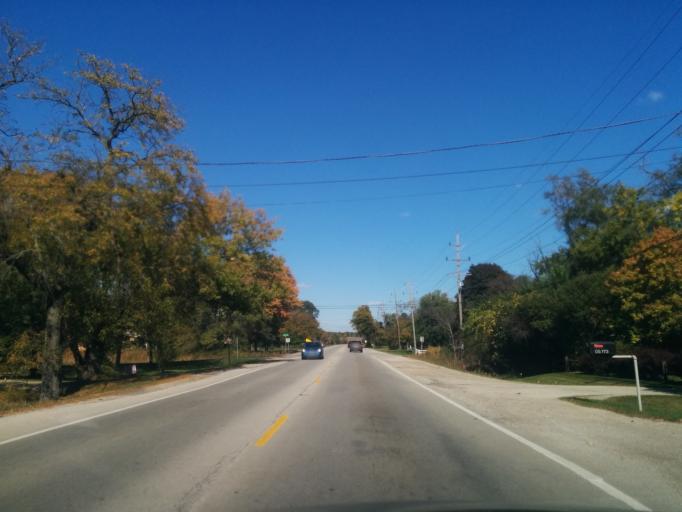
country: US
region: Illinois
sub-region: DuPage County
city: Lombard
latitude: 41.8717
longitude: -88.0330
